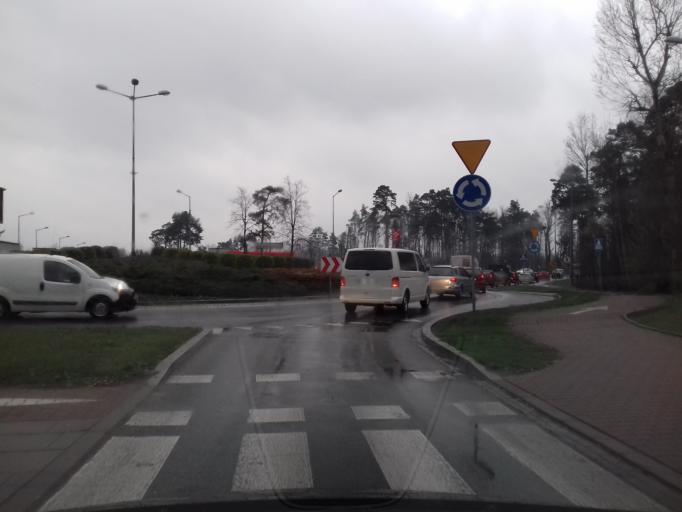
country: PL
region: Lesser Poland Voivodeship
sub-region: Powiat nowosadecki
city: Stary Sacz
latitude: 49.5667
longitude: 20.6568
